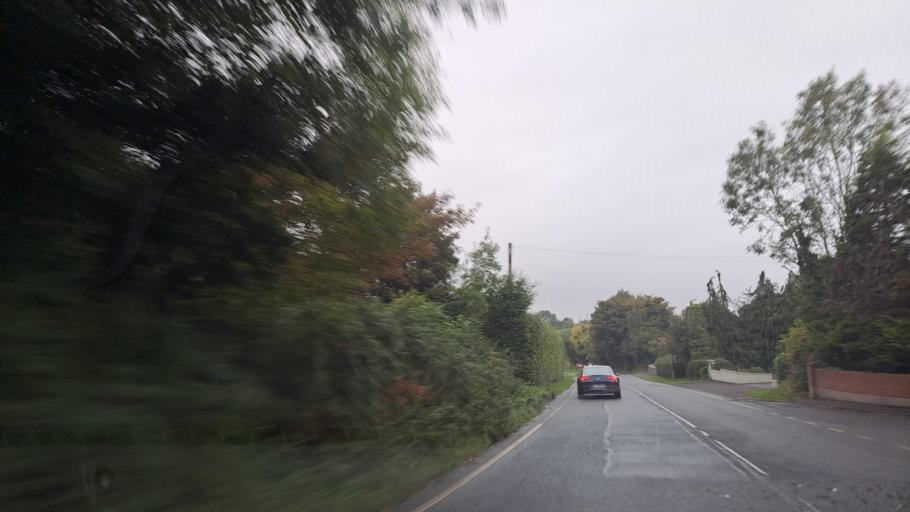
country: IE
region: Ulster
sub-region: County Monaghan
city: Monaghan
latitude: 54.2301
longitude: -6.9572
